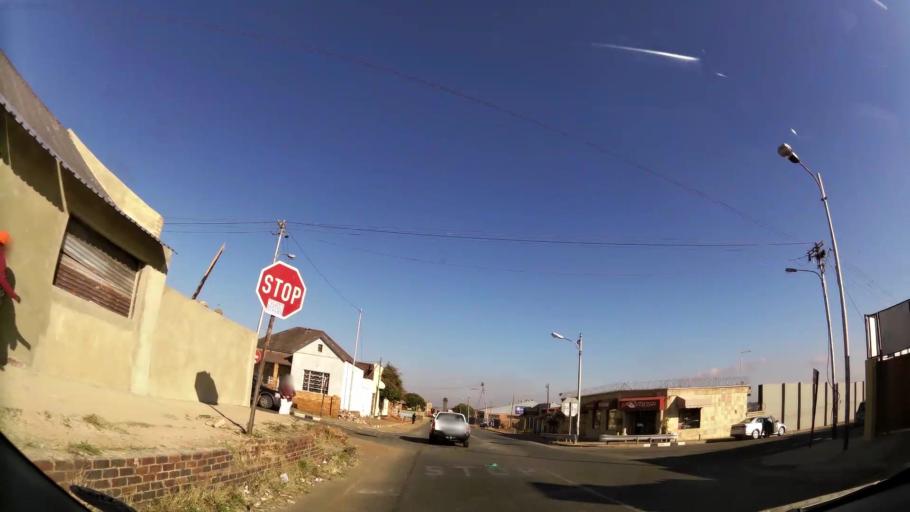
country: ZA
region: Gauteng
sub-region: City of Johannesburg Metropolitan Municipality
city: Roodepoort
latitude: -26.1627
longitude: 27.8628
